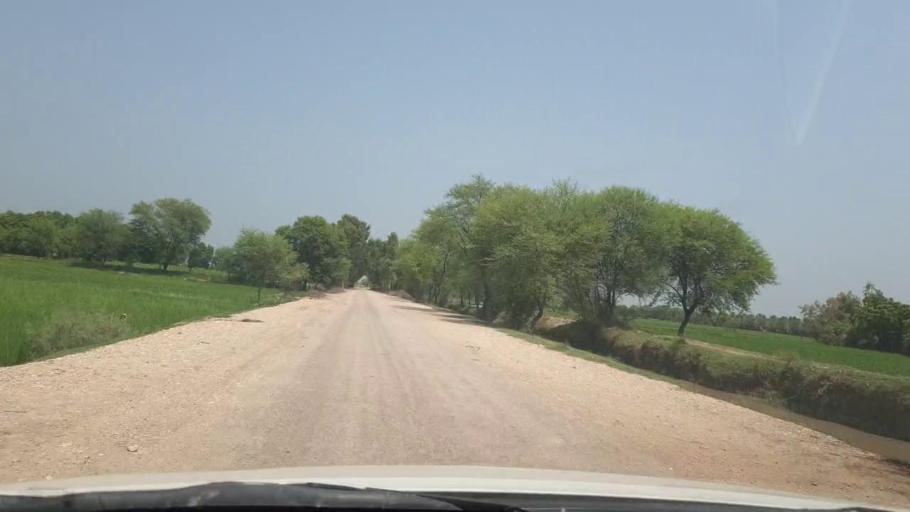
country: PK
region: Sindh
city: Rustam jo Goth
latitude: 28.0273
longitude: 68.7625
